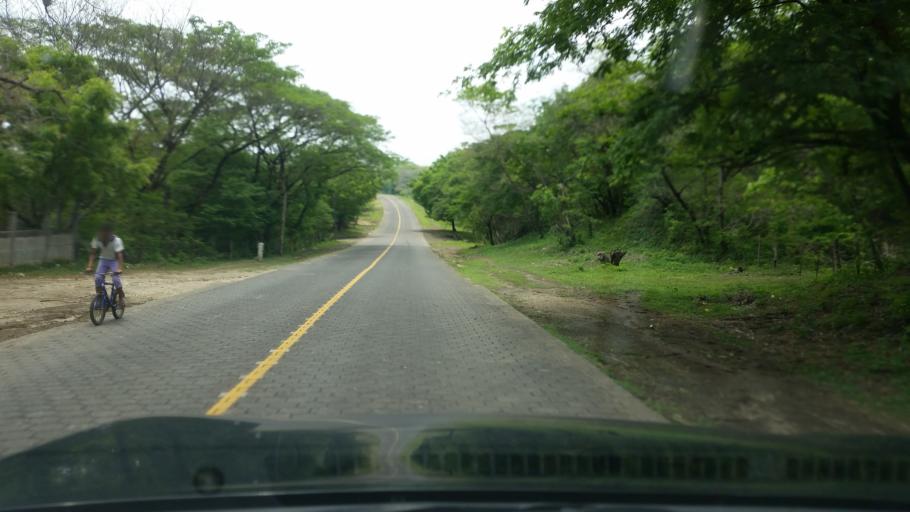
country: NI
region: Managua
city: Carlos Fonseca Amador
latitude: 11.9336
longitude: -86.5071
